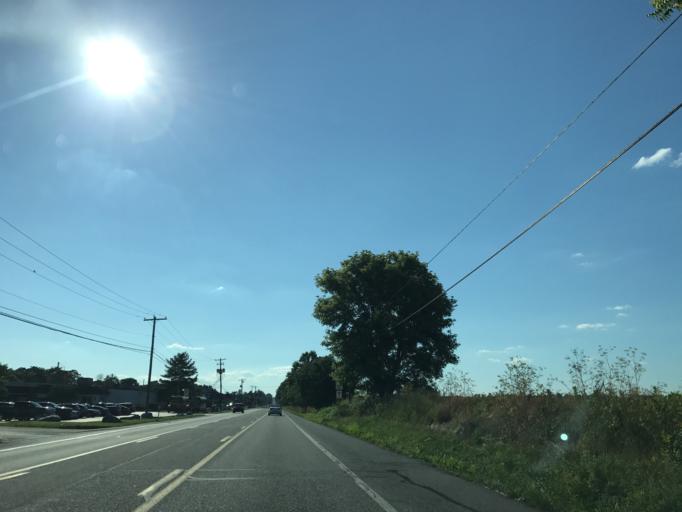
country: US
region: Pennsylvania
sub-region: Lancaster County
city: Rheems
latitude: 40.1290
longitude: -76.5567
